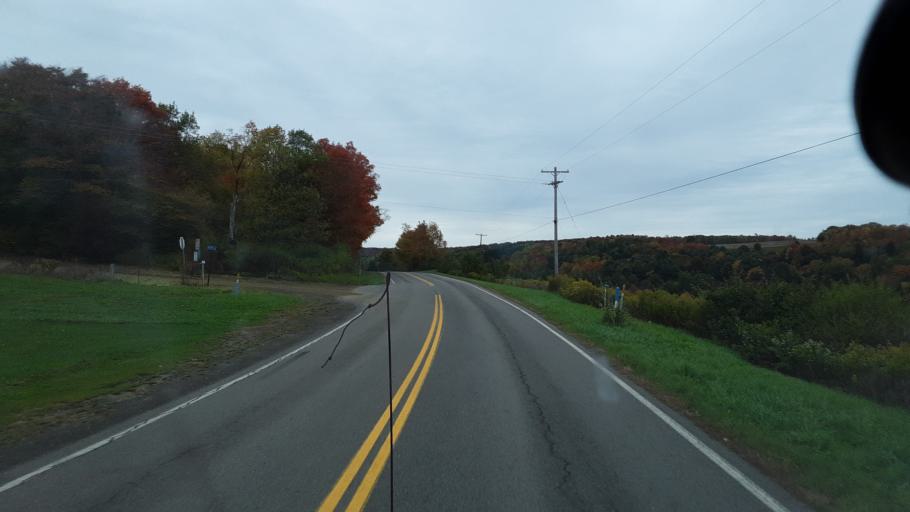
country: US
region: New York
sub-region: Allegany County
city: Andover
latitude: 42.0848
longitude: -77.7967
